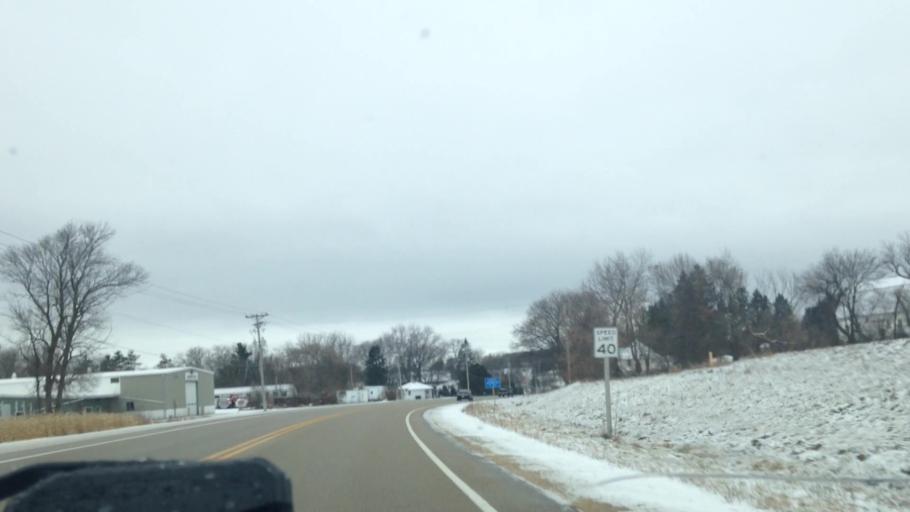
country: US
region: Wisconsin
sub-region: Dodge County
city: Beaver Dam
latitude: 43.4505
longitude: -88.7982
